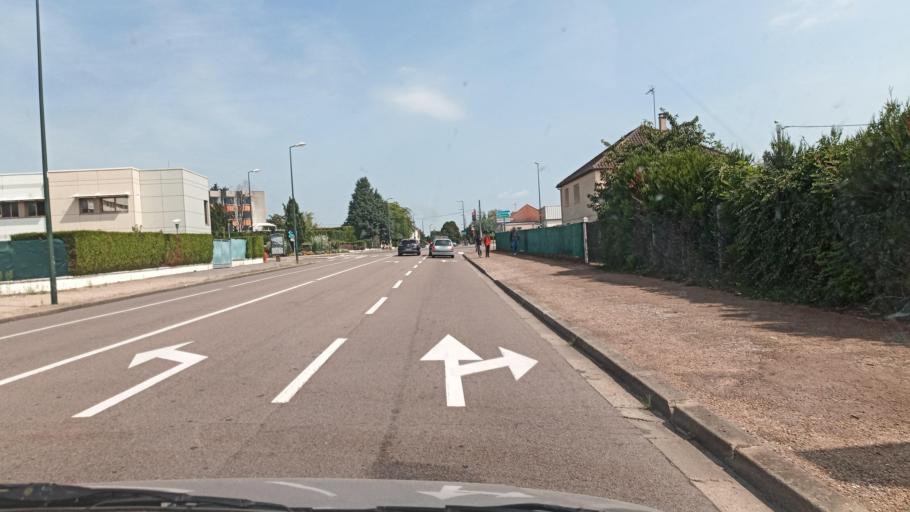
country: FR
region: Bourgogne
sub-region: Departement de l'Yonne
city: Sens
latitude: 48.1934
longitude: 3.3003
